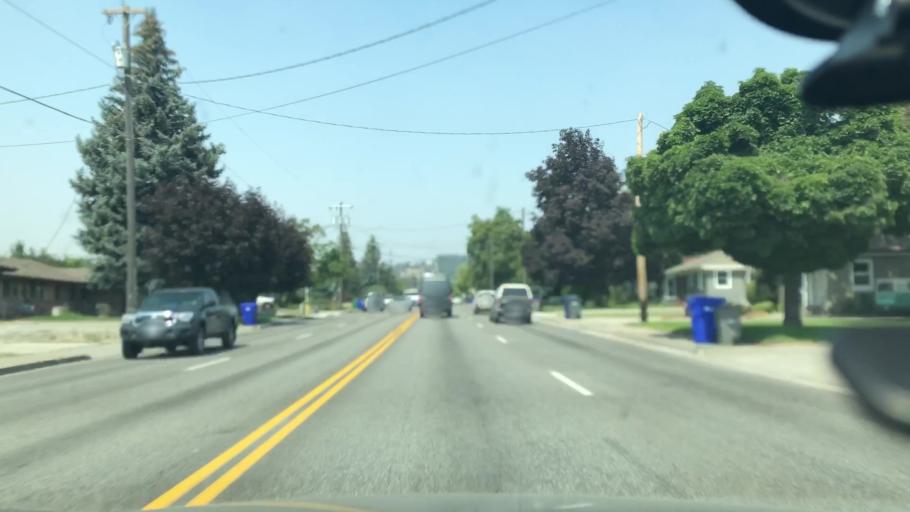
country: US
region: Washington
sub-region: Spokane County
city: Millwood
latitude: 47.6937
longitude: -117.2828
